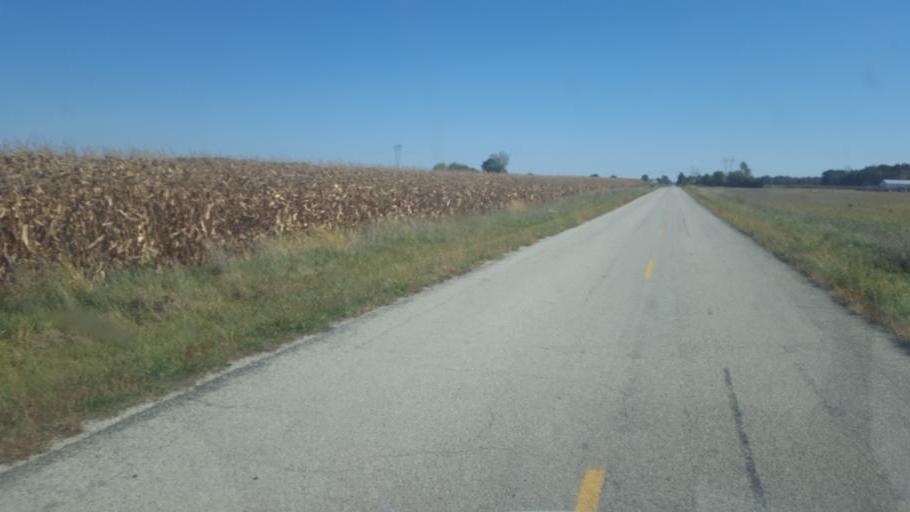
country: US
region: Ohio
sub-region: Crawford County
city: Bucyrus
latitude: 40.8629
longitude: -83.0994
